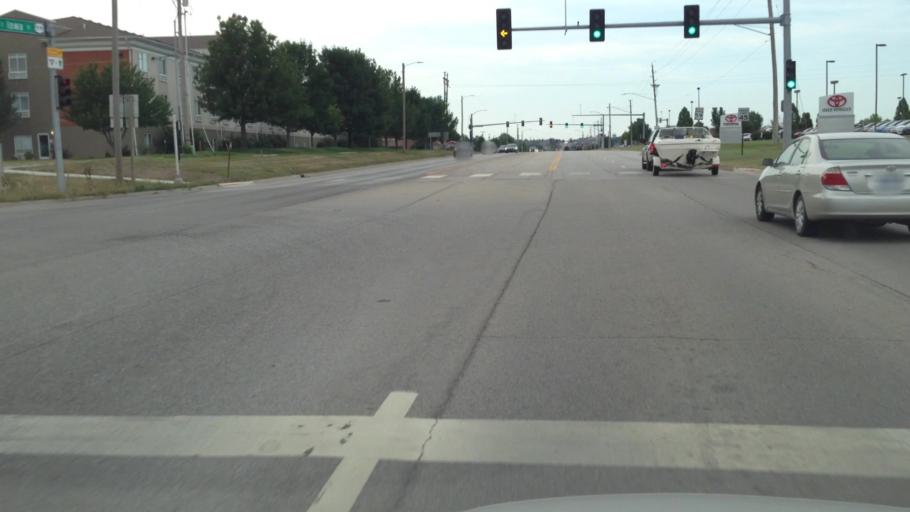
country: US
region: Kansas
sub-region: Douglas County
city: Lawrence
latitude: 38.9206
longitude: -95.2605
